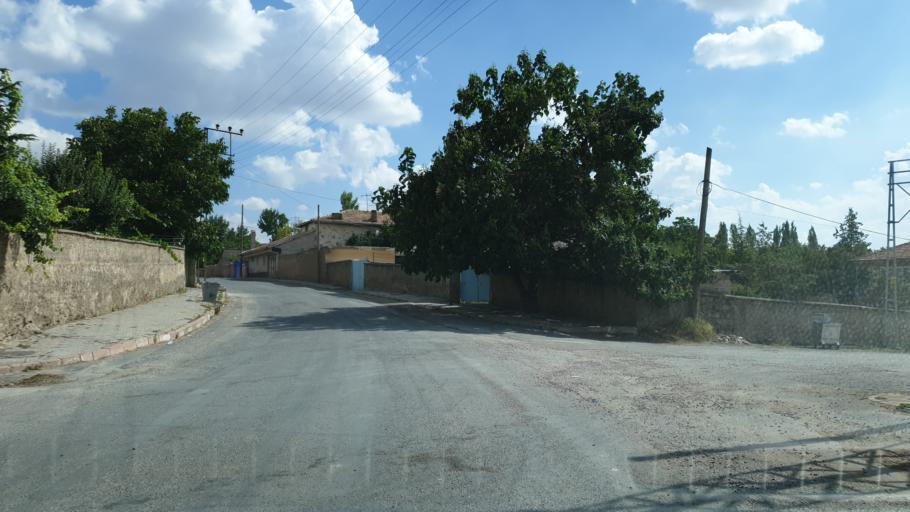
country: TR
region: Kayseri
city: Felahiye
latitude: 39.0902
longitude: 35.5630
